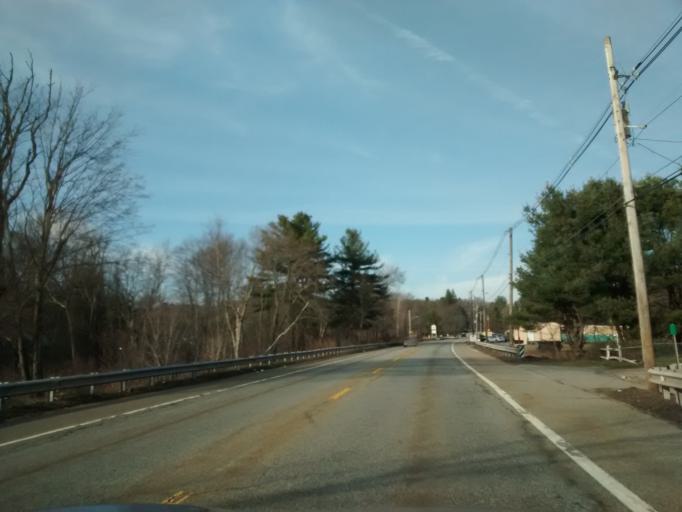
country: US
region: Massachusetts
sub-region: Worcester County
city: Charlton
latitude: 42.1397
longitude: -71.9984
